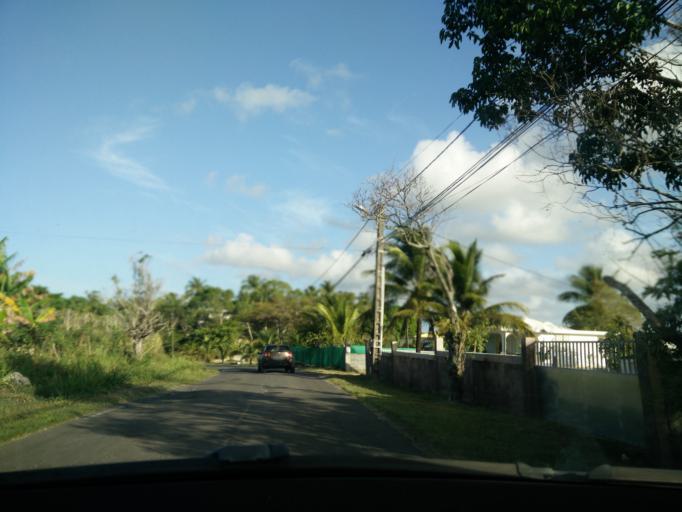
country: GP
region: Guadeloupe
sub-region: Guadeloupe
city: Sainte-Anne
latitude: 16.2775
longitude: -61.3997
